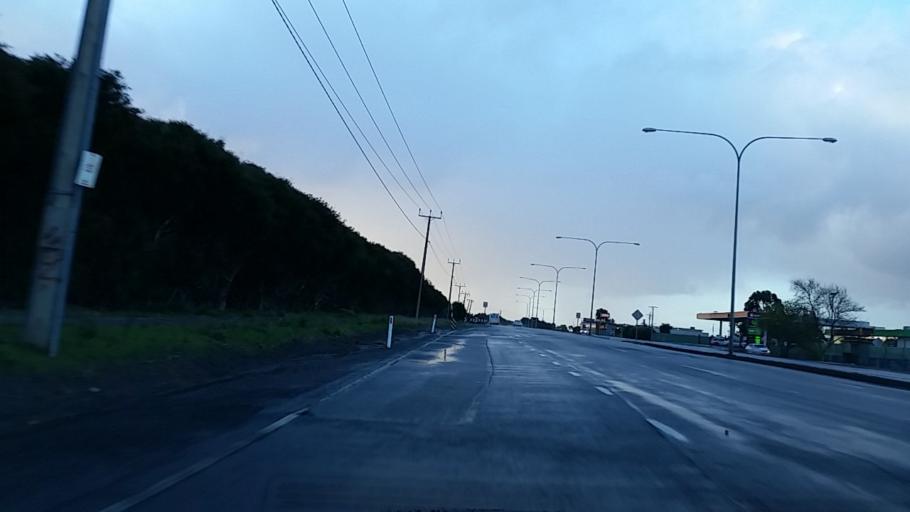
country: AU
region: South Australia
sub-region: Onkaparinga
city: Bedford Park
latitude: -35.0530
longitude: 138.5593
